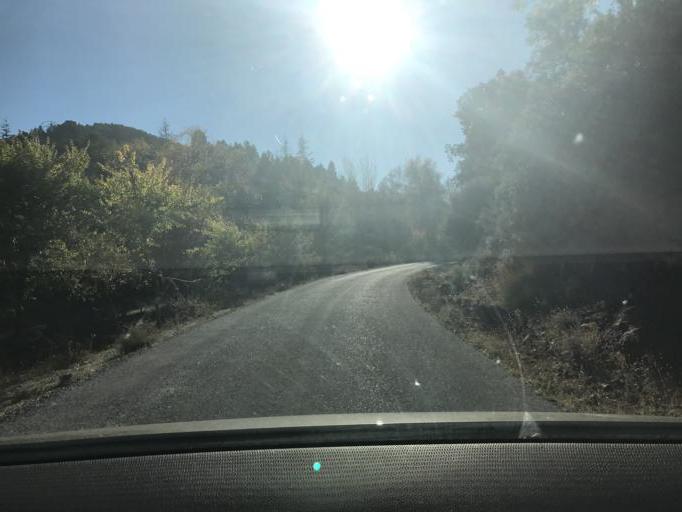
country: ES
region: Andalusia
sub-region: Provincia de Granada
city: Beas de Granada
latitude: 37.2942
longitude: -3.4816
